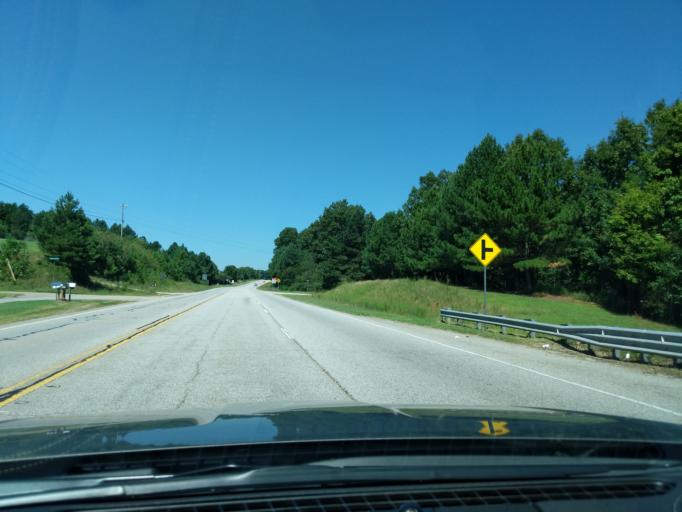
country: US
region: Georgia
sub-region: Habersham County
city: Demorest
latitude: 34.5775
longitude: -83.5990
